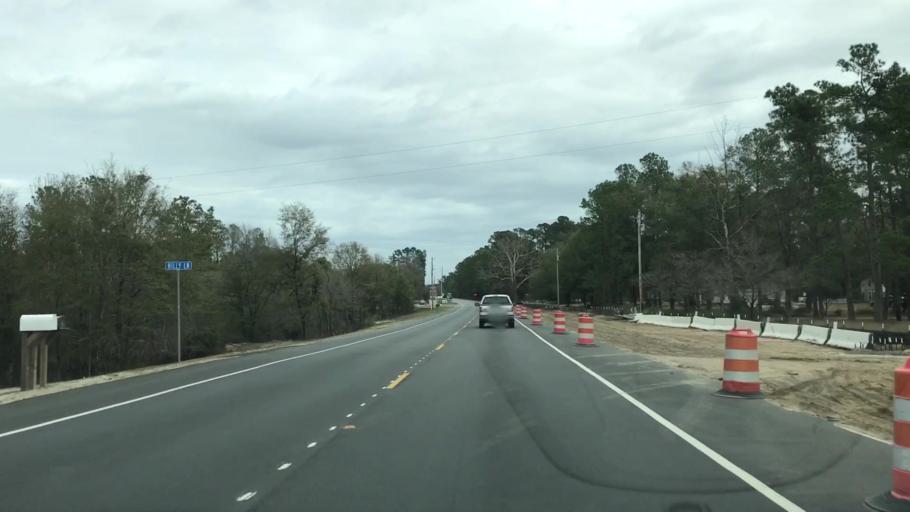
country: US
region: South Carolina
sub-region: Horry County
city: Socastee
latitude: 33.6699
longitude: -79.1411
